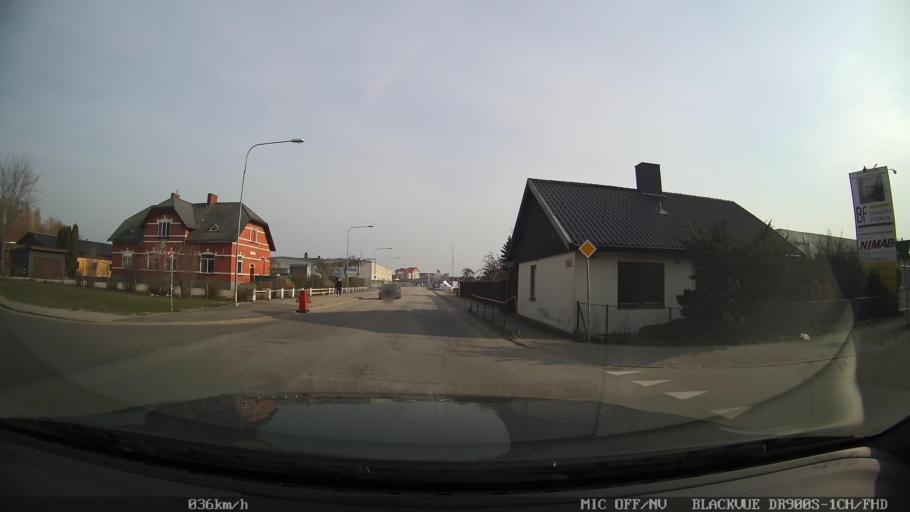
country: SE
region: Skane
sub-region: Ystads Kommun
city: Ystad
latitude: 55.4370
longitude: 13.8319
